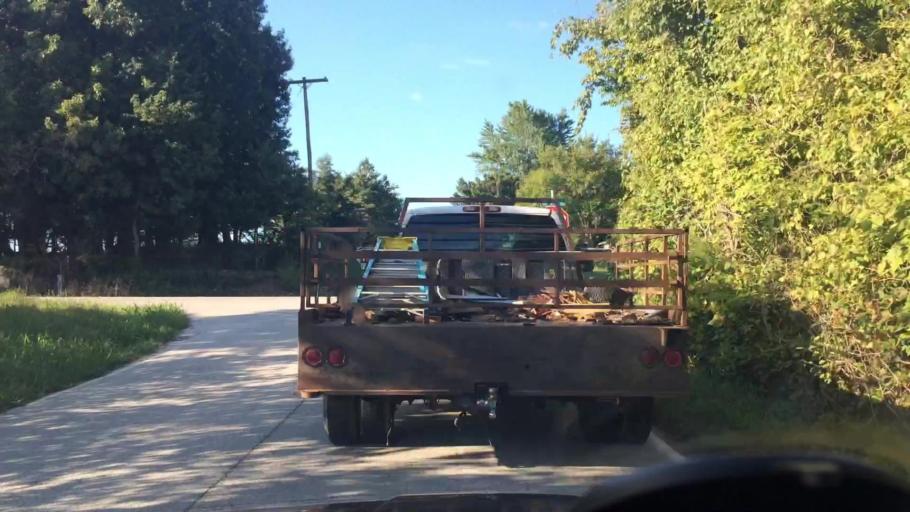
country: US
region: Missouri
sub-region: Greene County
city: Strafford
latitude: 37.2848
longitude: -93.0948
